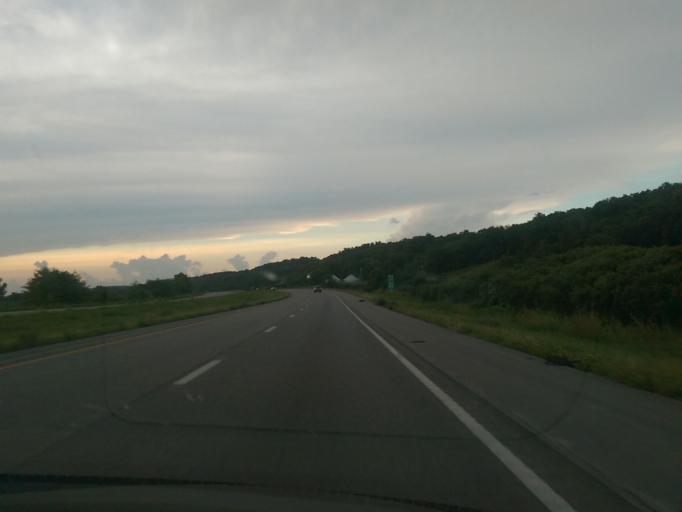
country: US
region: Missouri
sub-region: Atchison County
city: Rock Port
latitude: 40.3310
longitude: -95.4968
